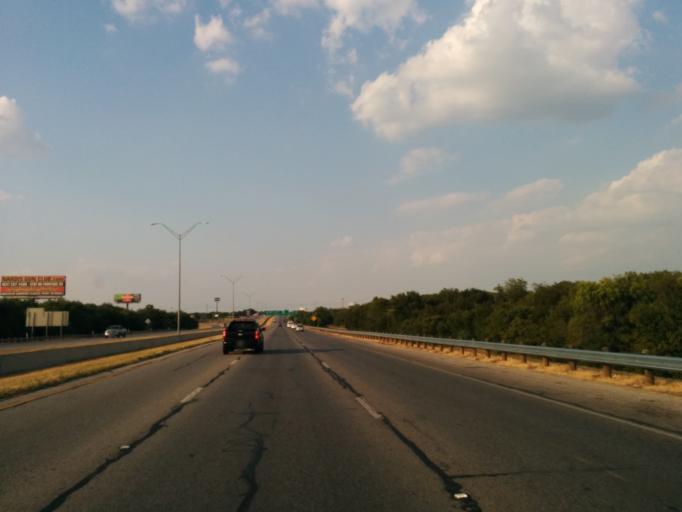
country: US
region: Texas
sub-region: Bexar County
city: Kirby
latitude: 29.4189
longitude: -98.4257
